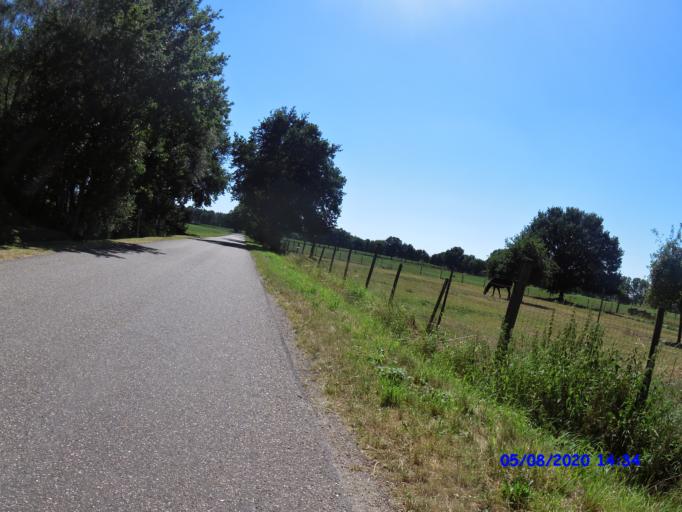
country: BE
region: Flanders
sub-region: Provincie Antwerpen
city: Rijkevorsel
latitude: 51.3632
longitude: 4.7729
